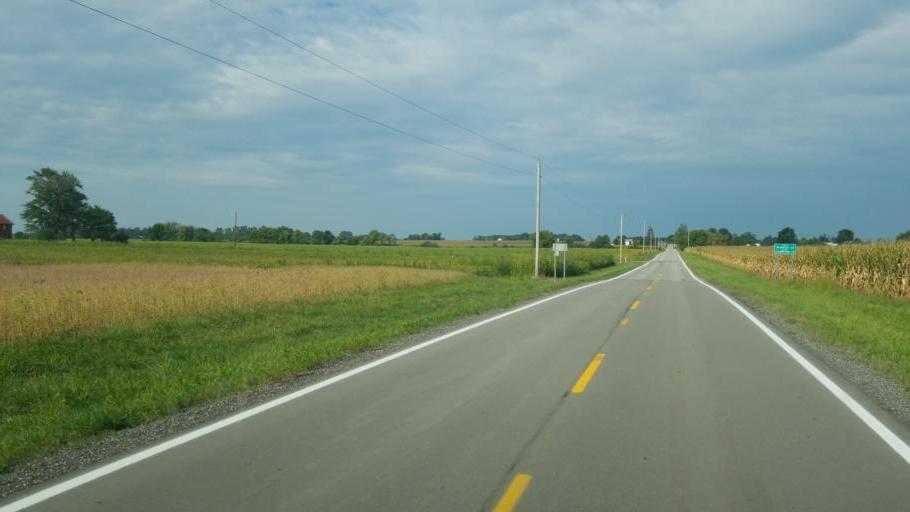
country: US
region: Ohio
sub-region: Marion County
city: Marion
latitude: 40.7174
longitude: -83.1110
